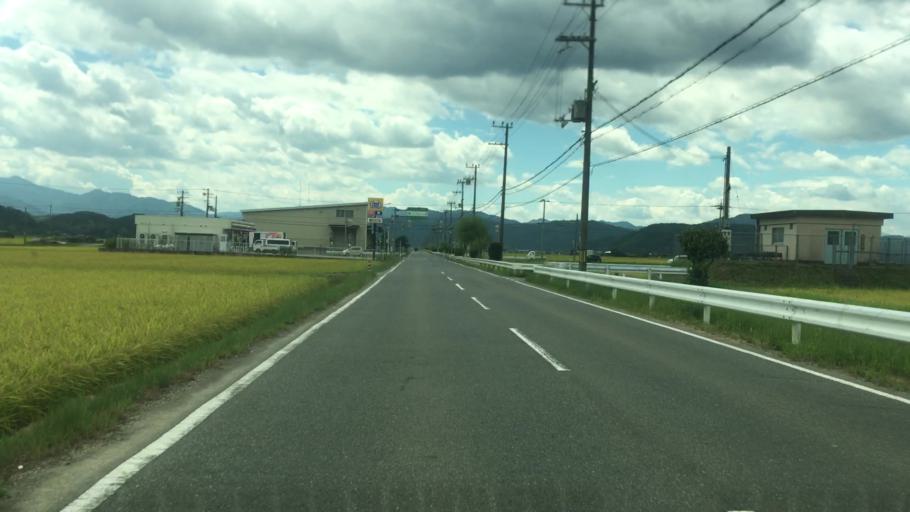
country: JP
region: Hyogo
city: Toyooka
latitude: 35.5261
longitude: 134.8398
